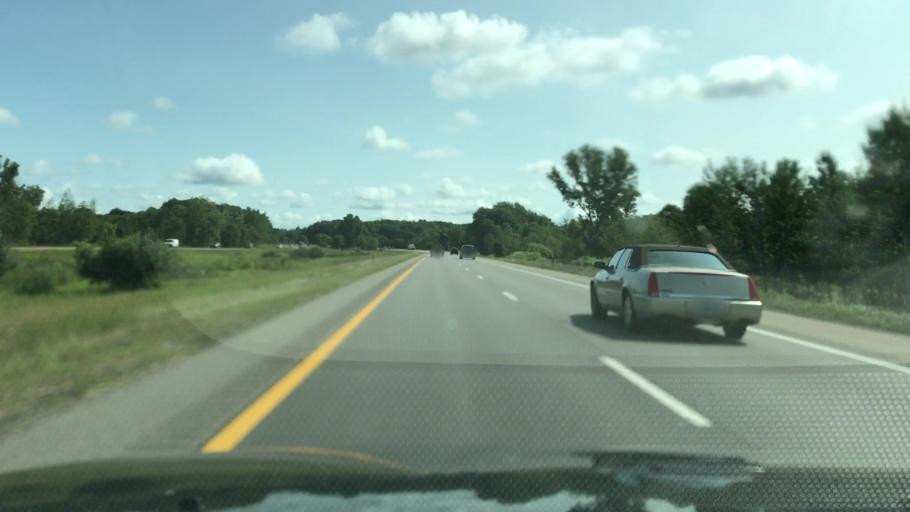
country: US
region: Michigan
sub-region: Kent County
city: Cedar Springs
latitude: 43.3117
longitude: -85.5276
